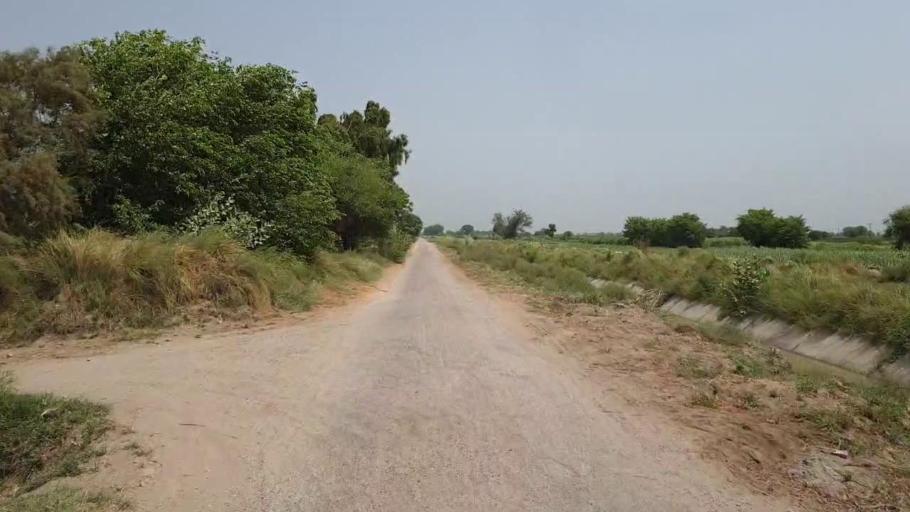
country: PK
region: Sindh
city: Nawabshah
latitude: 26.2764
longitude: 68.3135
